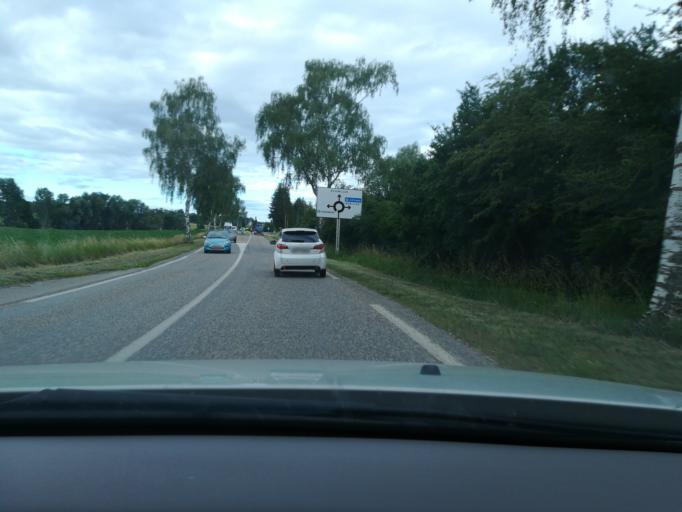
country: FR
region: Alsace
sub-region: Departement du Bas-Rhin
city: Bouxwiller
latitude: 48.8328
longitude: 7.4985
